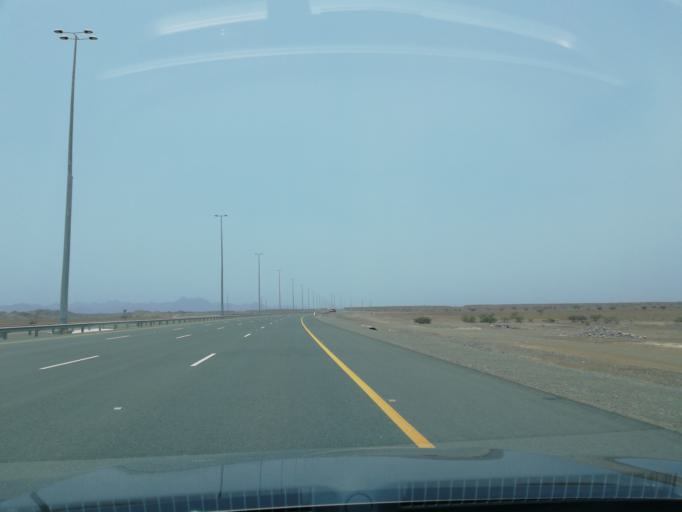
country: OM
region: Al Batinah
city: Al Liwa'
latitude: 24.5592
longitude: 56.4686
